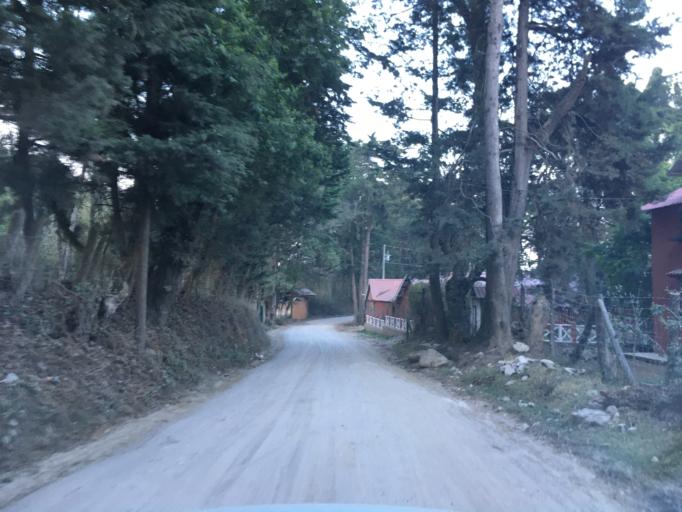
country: GT
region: Chimaltenango
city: Tecpan Guatemala
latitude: 14.7585
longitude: -91.0050
